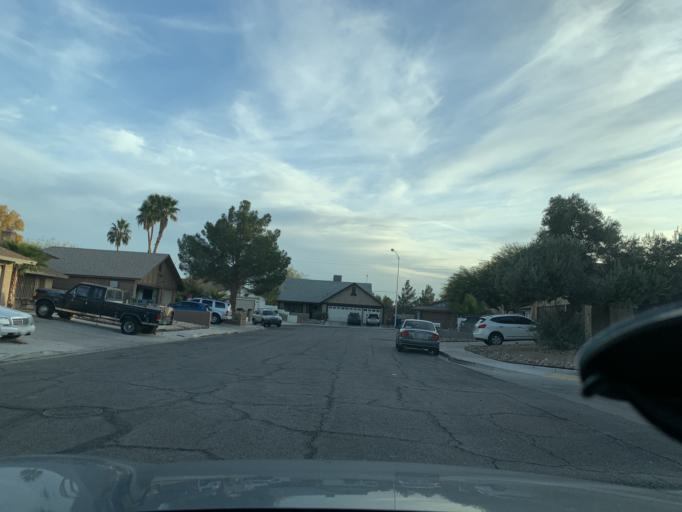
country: US
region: Nevada
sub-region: Clark County
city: Spring Valley
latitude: 36.0936
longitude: -115.2257
